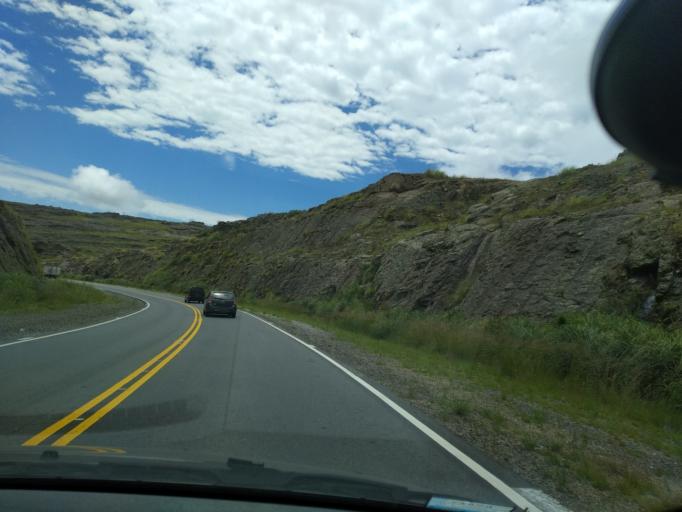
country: AR
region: Cordoba
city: Cuesta Blanca
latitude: -31.6017
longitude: -64.7115
